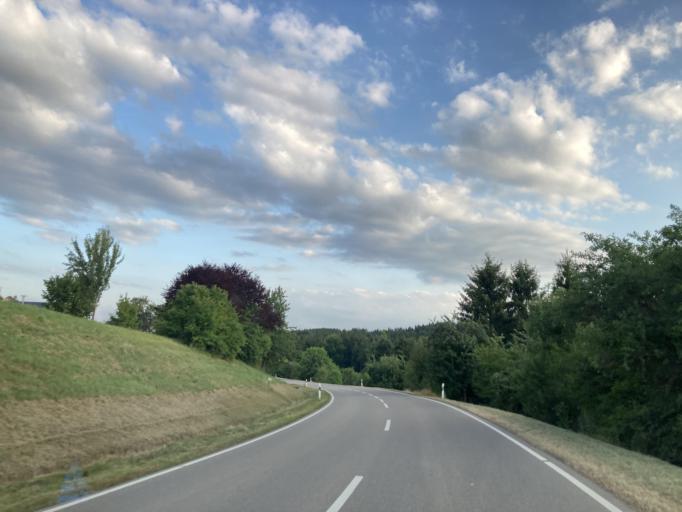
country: DE
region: Baden-Wuerttemberg
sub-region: Karlsruhe Region
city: Dornstetten
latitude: 48.4622
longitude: 8.5049
